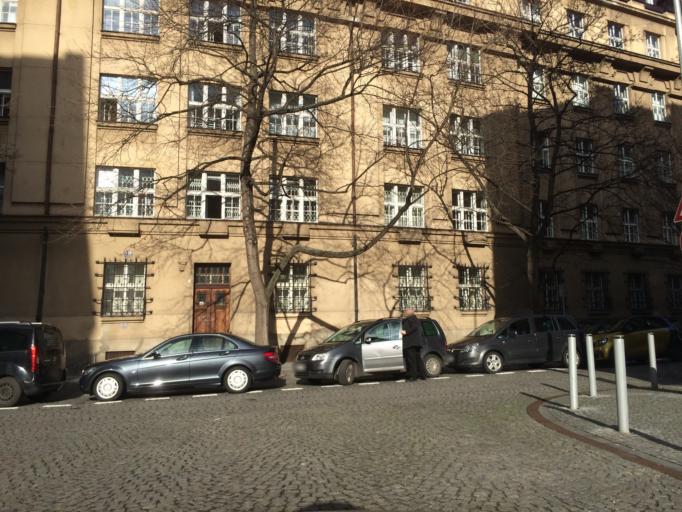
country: CZ
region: Praha
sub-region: Praha 1
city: Mala Strana
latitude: 50.0995
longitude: 14.3992
